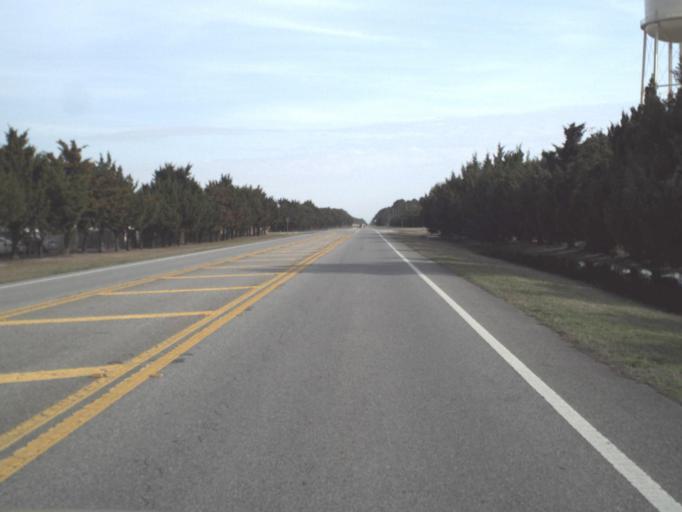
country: US
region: Florida
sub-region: Bay County
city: Tyndall Air Force Base
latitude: 30.0678
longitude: -85.5875
